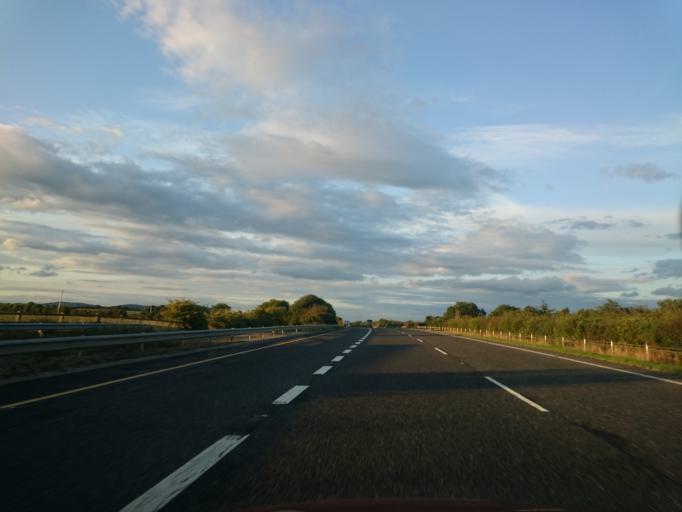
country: IE
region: Leinster
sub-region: Loch Garman
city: Castletown
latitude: 52.7700
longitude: -6.1874
